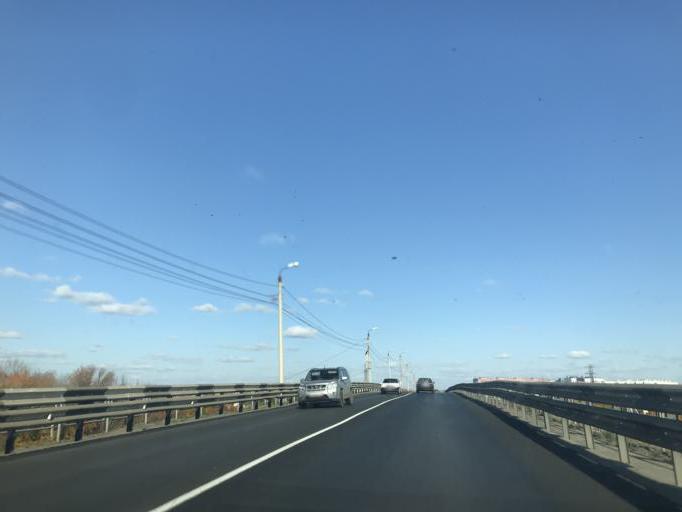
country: RU
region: Chelyabinsk
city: Roshchino
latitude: 55.2324
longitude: 61.2917
